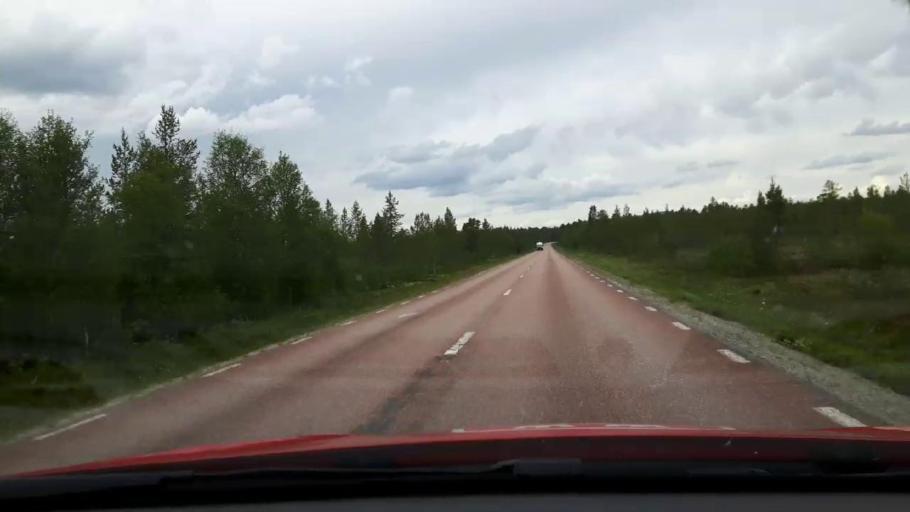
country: NO
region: Hedmark
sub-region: Engerdal
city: Engerdal
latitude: 62.4883
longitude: 12.6478
